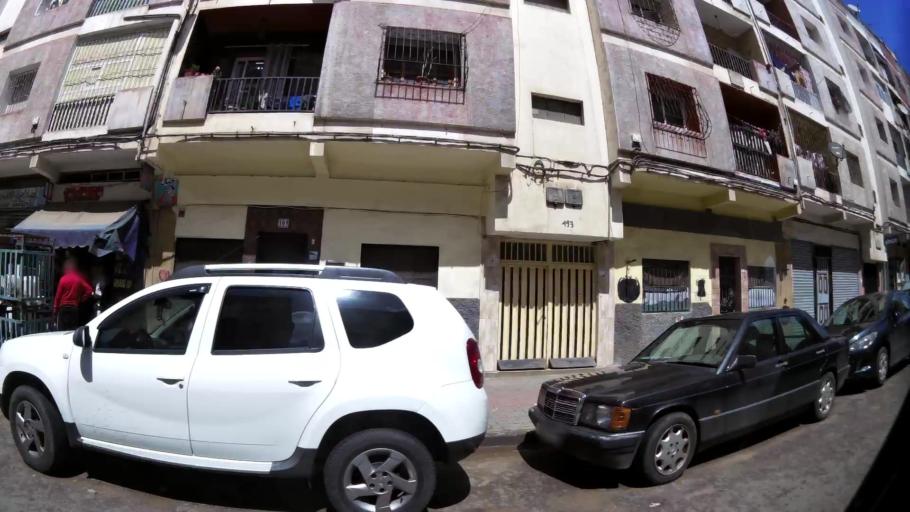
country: MA
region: Grand Casablanca
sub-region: Mediouna
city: Tit Mellil
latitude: 33.5403
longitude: -7.5516
